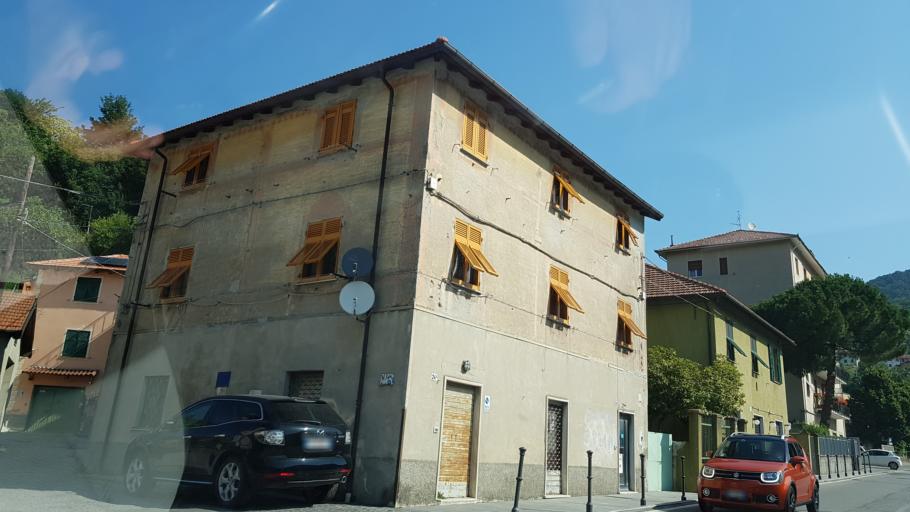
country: IT
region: Liguria
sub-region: Provincia di Genova
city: Serra Ricco
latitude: 44.5108
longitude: 8.9388
